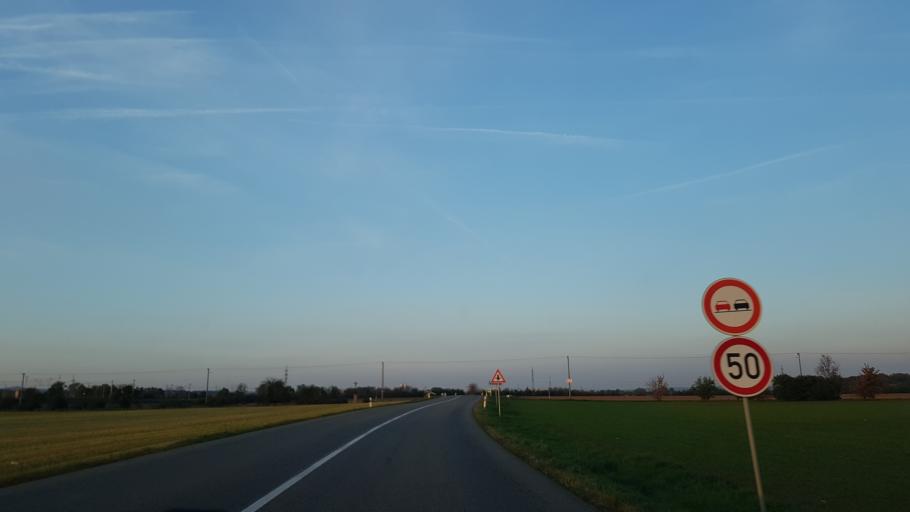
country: CZ
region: Zlin
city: Nedakonice
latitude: 49.0495
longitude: 17.3966
